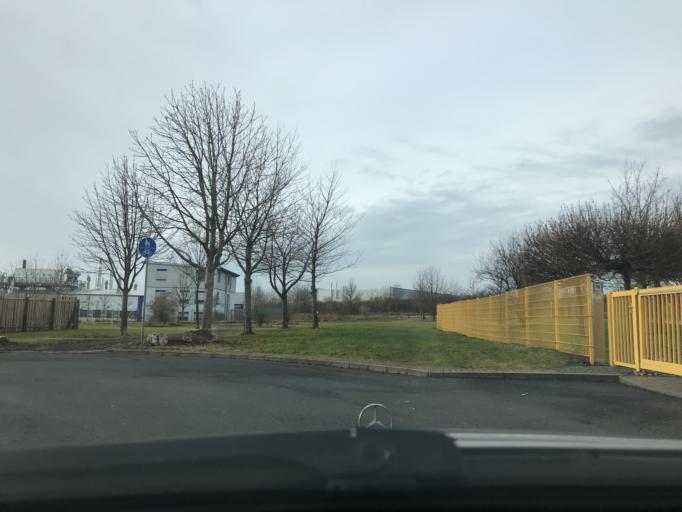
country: DE
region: Thuringia
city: Muehlhausen
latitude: 51.1955
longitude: 10.4790
